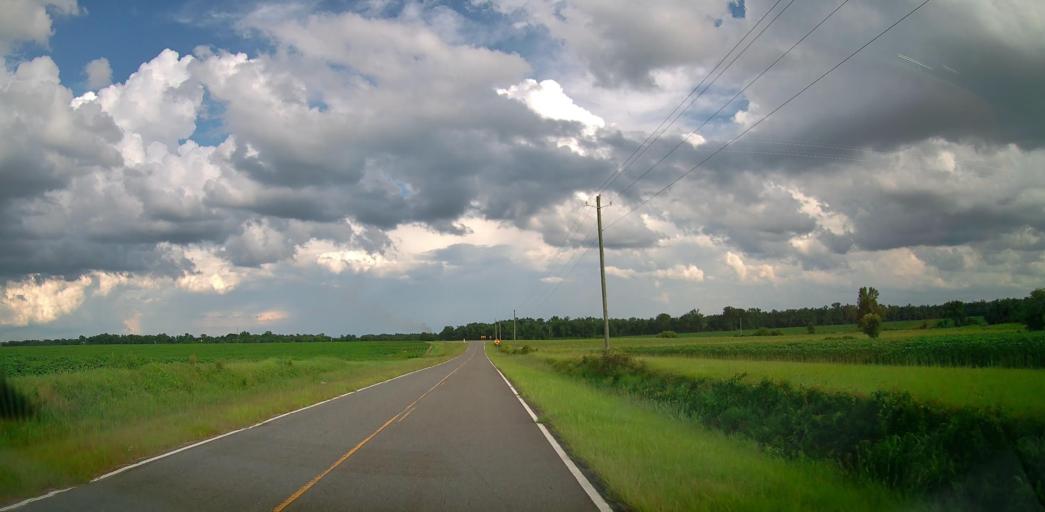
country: US
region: Georgia
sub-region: Bleckley County
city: Cochran
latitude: 32.4051
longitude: -83.4240
